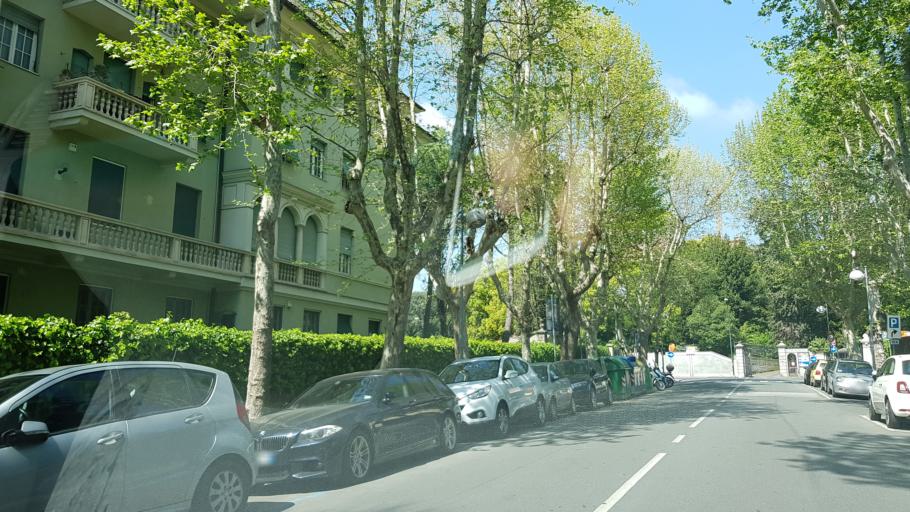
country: IT
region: Liguria
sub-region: Provincia di Genova
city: Genoa
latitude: 44.3951
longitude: 8.9731
